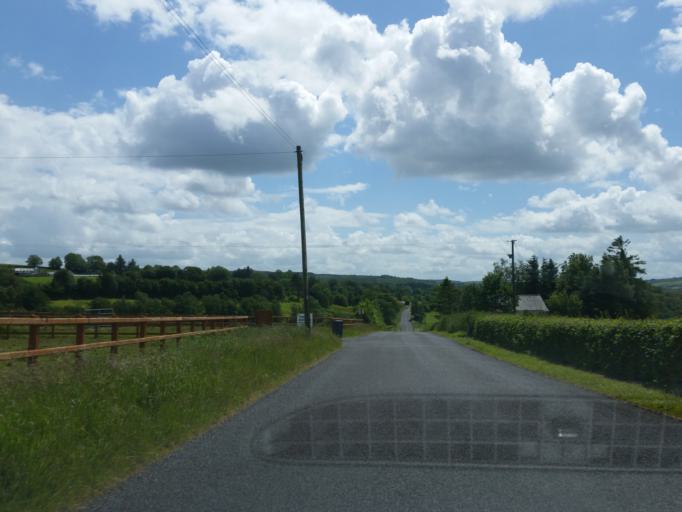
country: GB
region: Northern Ireland
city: Fivemiletown
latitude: 54.3468
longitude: -7.2966
